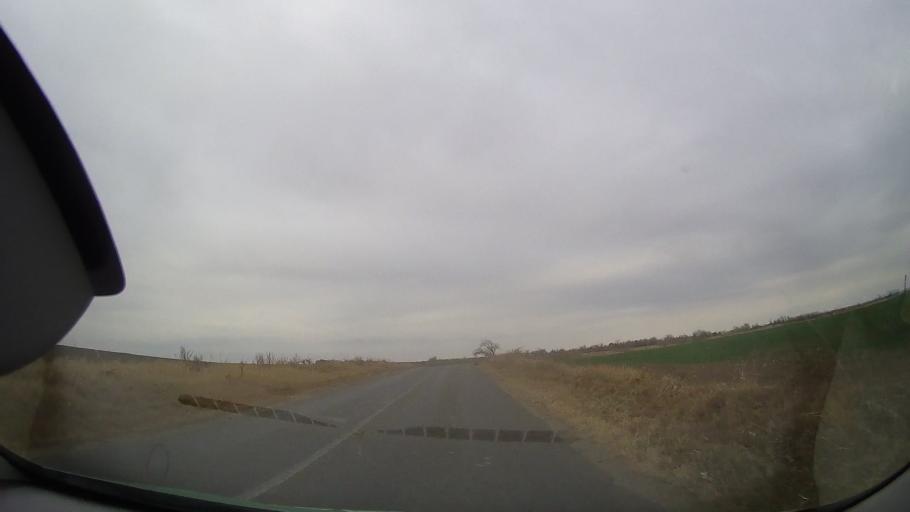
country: RO
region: Buzau
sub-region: Comuna Rusetu
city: Rusetu
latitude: 44.9685
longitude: 27.1876
